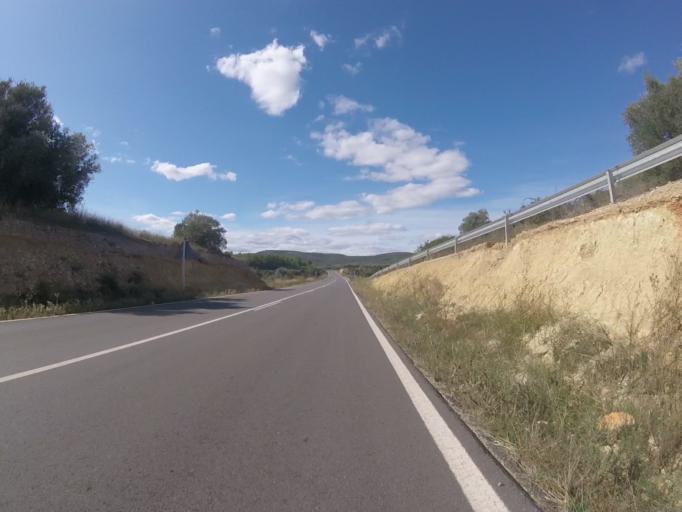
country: ES
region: Valencia
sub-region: Provincia de Castello
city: Chert/Xert
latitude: 40.4269
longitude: 0.1536
